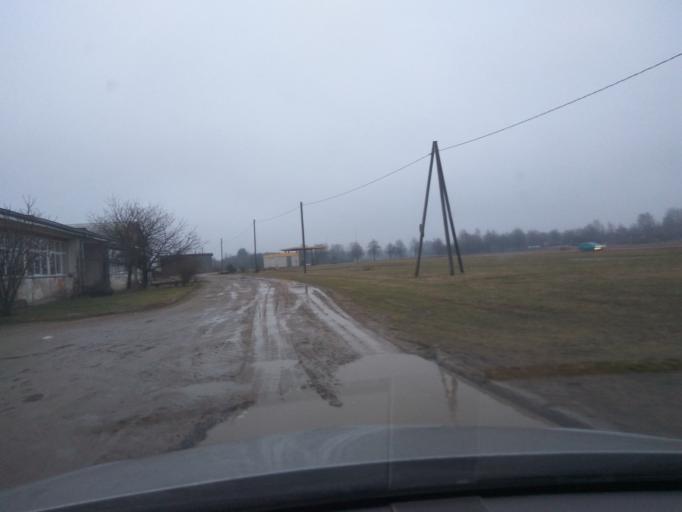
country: LV
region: Aizpute
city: Aizpute
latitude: 56.8383
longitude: 21.7610
